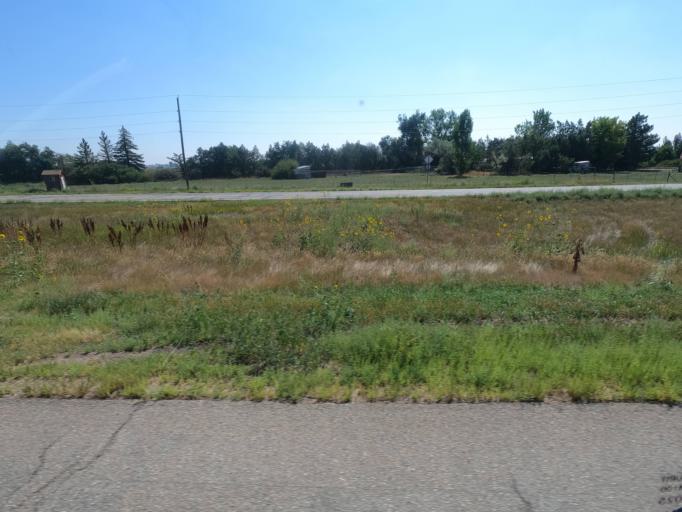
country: US
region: Colorado
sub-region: Larimer County
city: Fort Collins
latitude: 40.6080
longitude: -105.0011
